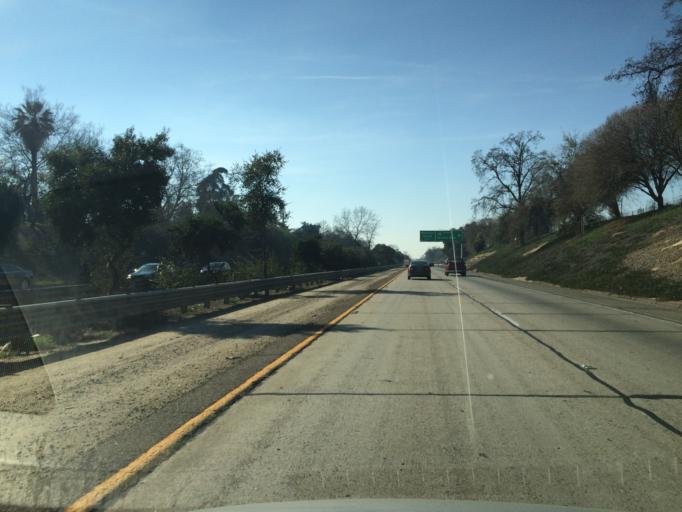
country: US
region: California
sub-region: Tulare County
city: Visalia
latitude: 36.3271
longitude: -119.3053
